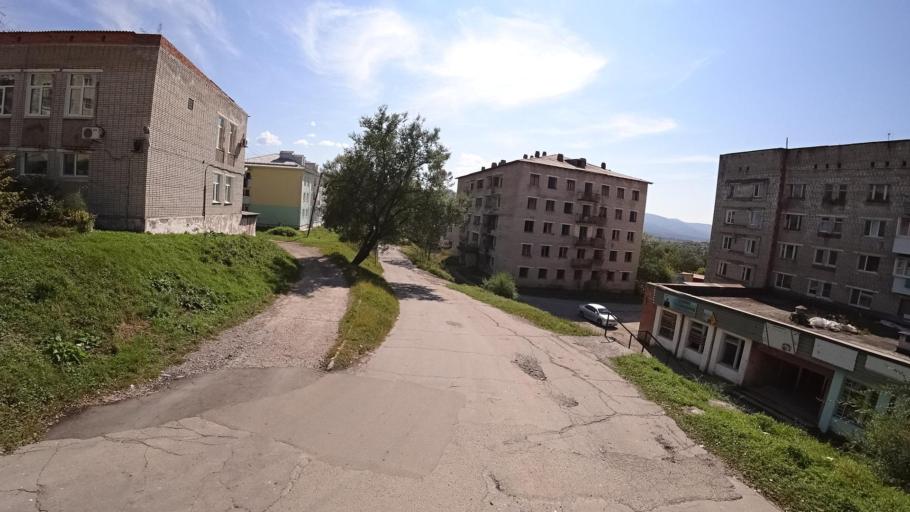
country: RU
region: Jewish Autonomous Oblast
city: Londoko
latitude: 49.0131
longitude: 131.8829
